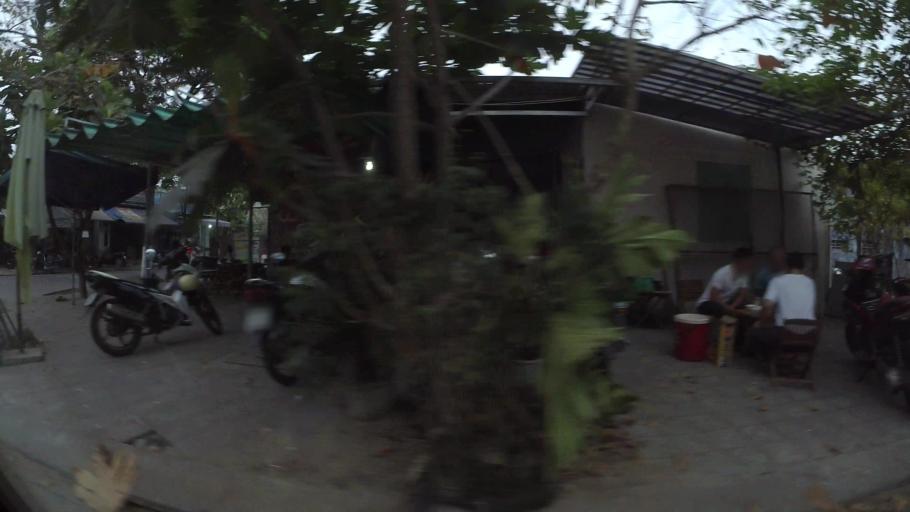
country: VN
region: Da Nang
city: Thanh Khe
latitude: 16.0497
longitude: 108.1766
